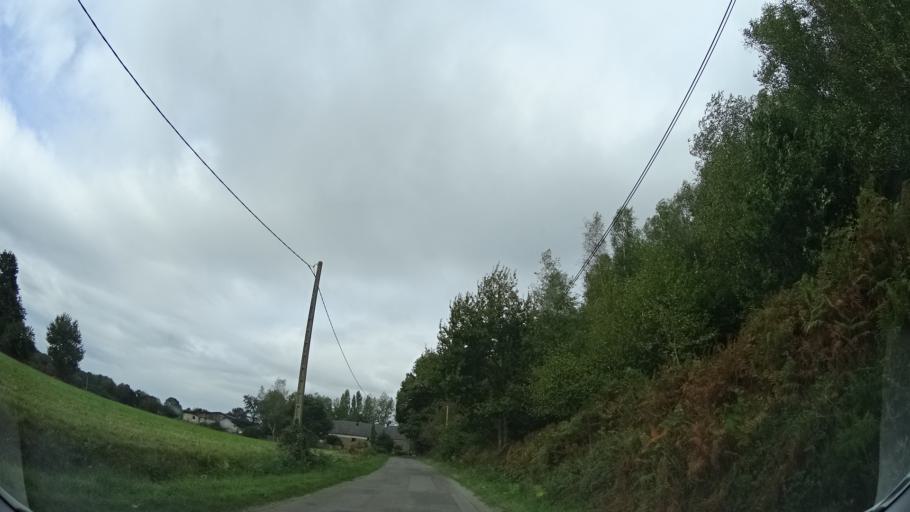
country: FR
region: Brittany
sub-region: Departement d'Ille-et-Vilaine
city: Tinteniac
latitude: 48.2913
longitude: -1.8719
